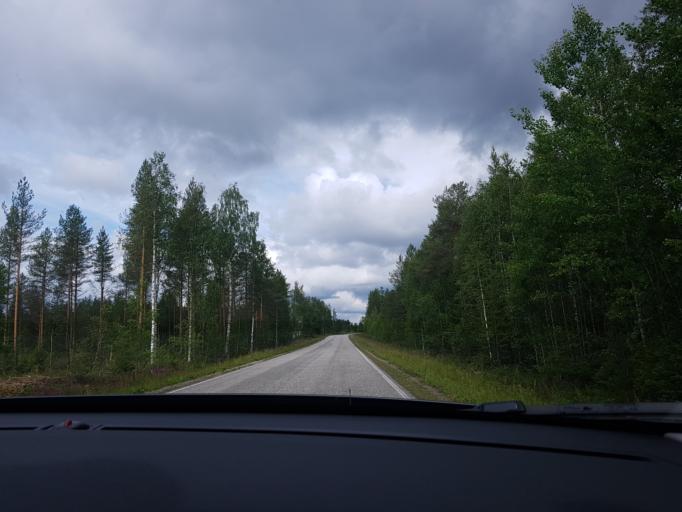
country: FI
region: Kainuu
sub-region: Kehys-Kainuu
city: Kuhmo
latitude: 64.2708
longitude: 29.3767
